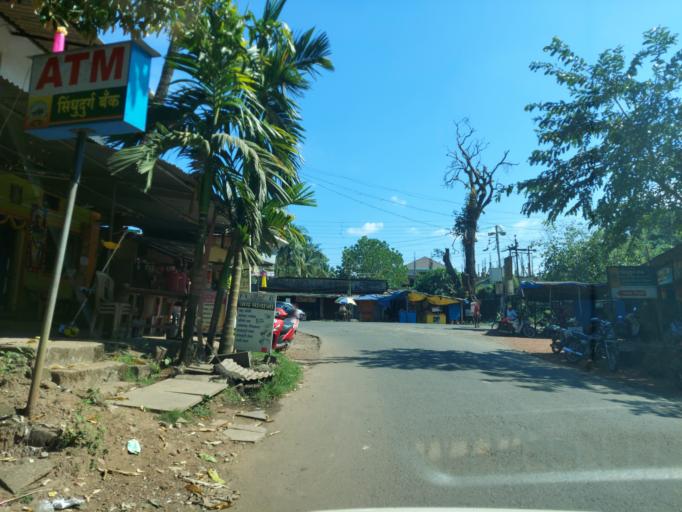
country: IN
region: Maharashtra
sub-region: Sindhudurg
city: Kudal
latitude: 15.9881
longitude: 73.6826
